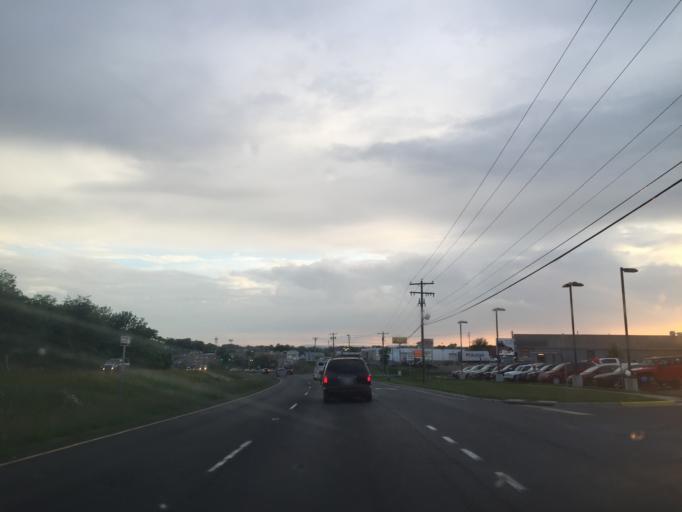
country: US
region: Virginia
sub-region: City of Winchester
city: Winchester
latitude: 39.1869
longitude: -78.1268
